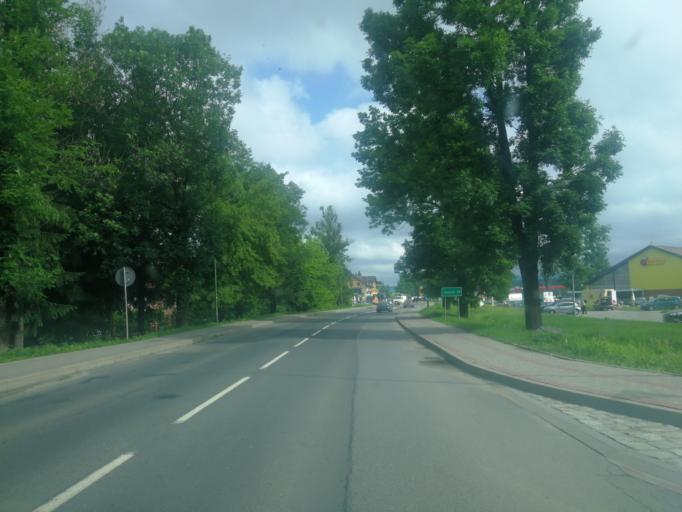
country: PL
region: Subcarpathian Voivodeship
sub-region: Powiat leski
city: Lesko
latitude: 49.4797
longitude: 22.3236
